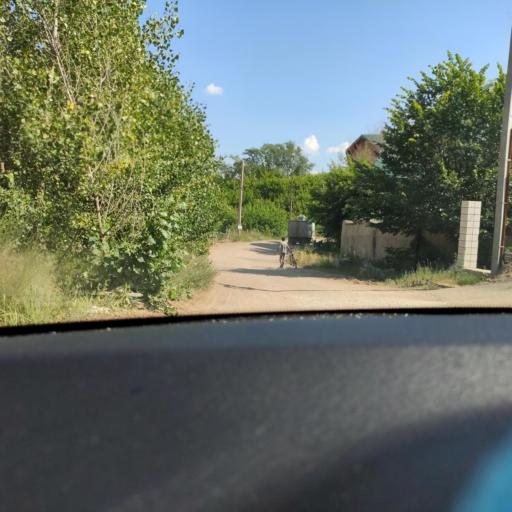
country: RU
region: Samara
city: Volzhskiy
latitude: 53.4374
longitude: 50.1656
